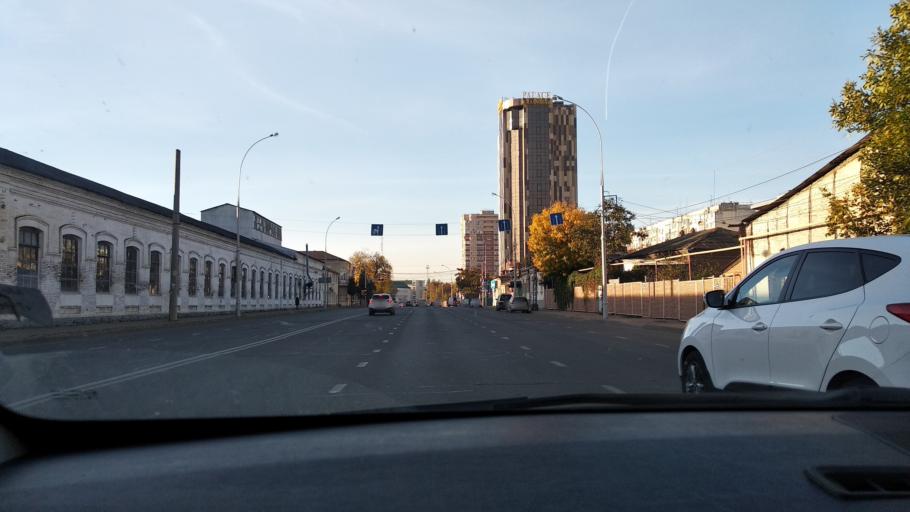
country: RU
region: Krasnodarskiy
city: Krasnodar
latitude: 45.0202
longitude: 38.9812
